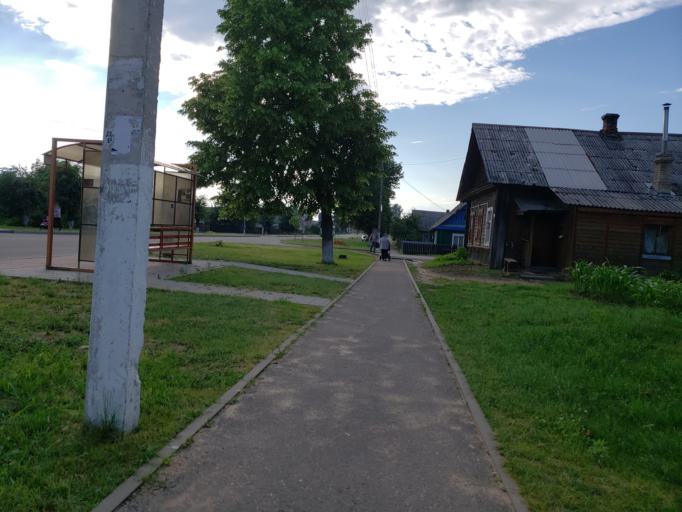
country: BY
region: Minsk
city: Chervyen'
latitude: 53.7062
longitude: 28.4344
